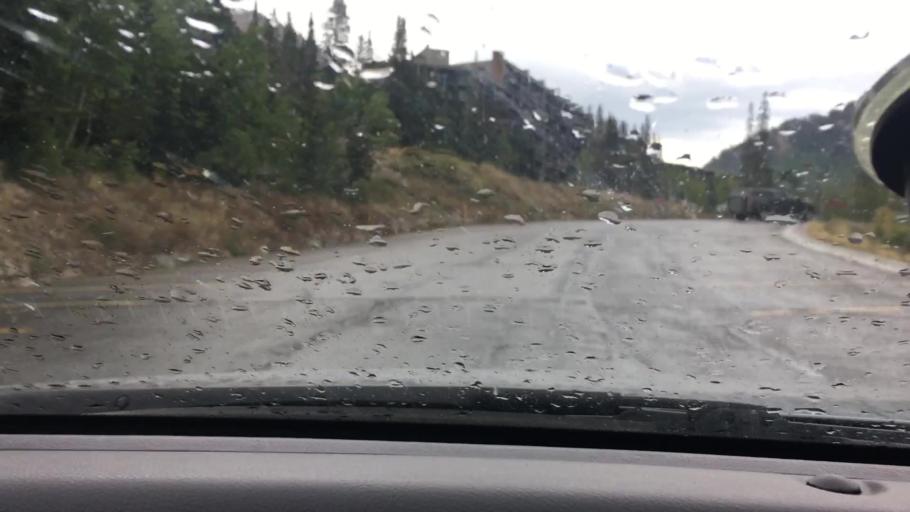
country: US
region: Utah
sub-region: Salt Lake County
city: Granite
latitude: 40.5798
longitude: -111.6635
